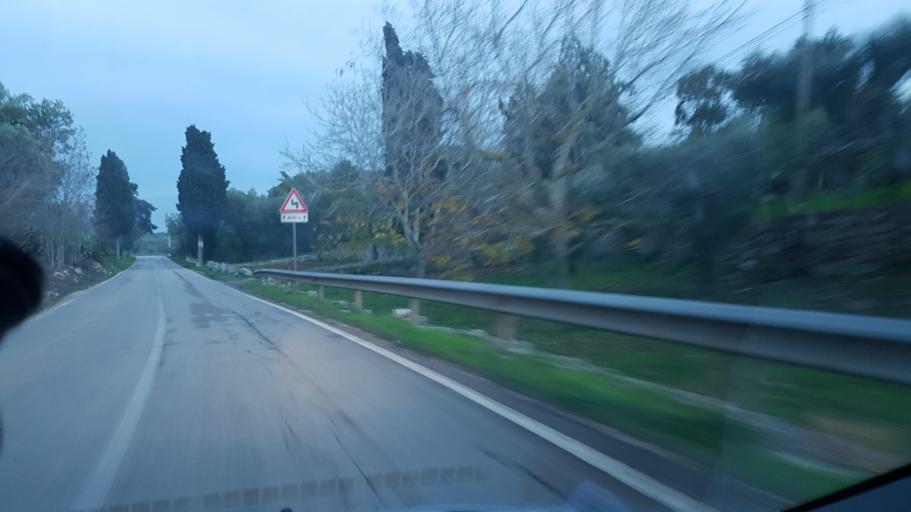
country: IT
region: Apulia
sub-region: Provincia di Brindisi
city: San Michele Salentino
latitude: 40.6417
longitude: 17.5774
